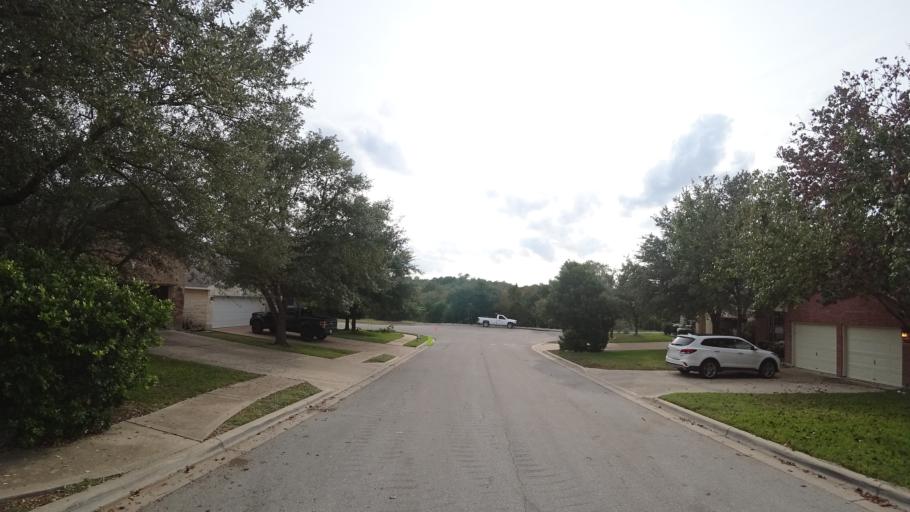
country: US
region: Texas
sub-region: Travis County
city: Hudson Bend
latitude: 30.3827
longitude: -97.8900
